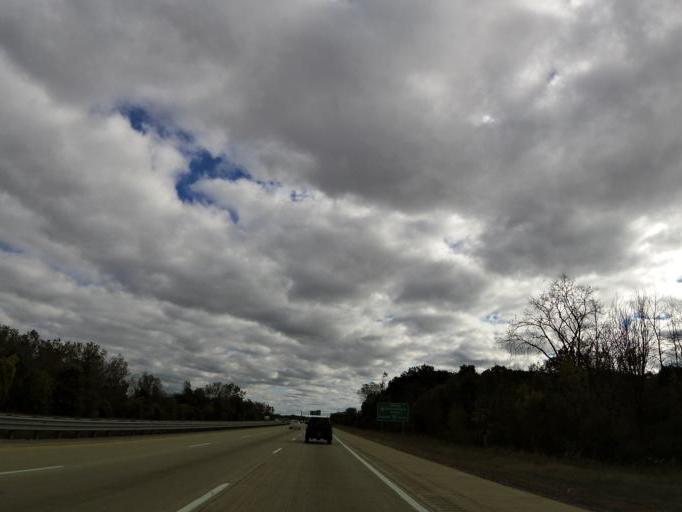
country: US
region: Michigan
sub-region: Genesee County
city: Flint
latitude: 42.9789
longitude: -83.7516
